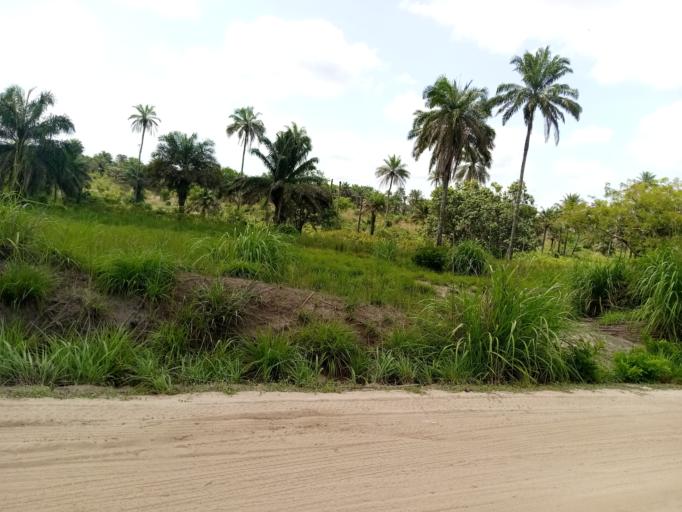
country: SL
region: Western Area
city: Waterloo
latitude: 8.3514
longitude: -13.0019
